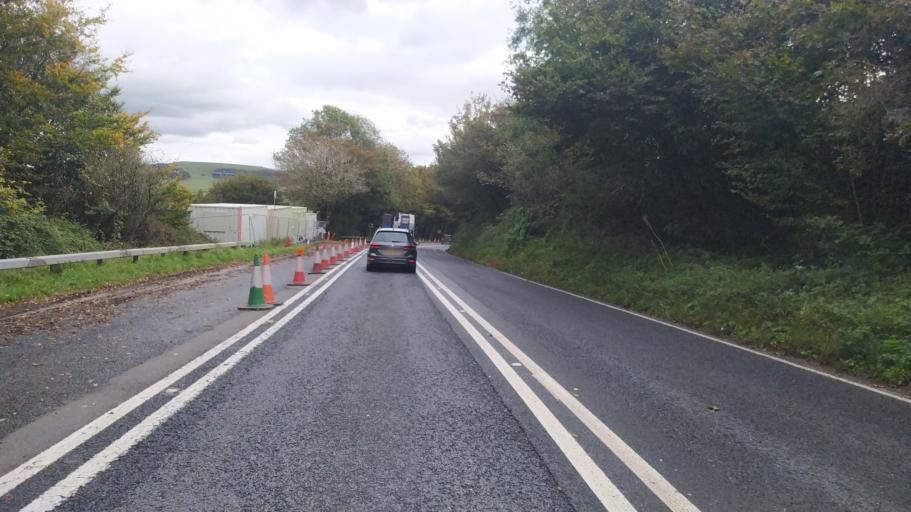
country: GB
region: England
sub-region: Dorset
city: Bridport
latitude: 50.7366
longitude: -2.8325
